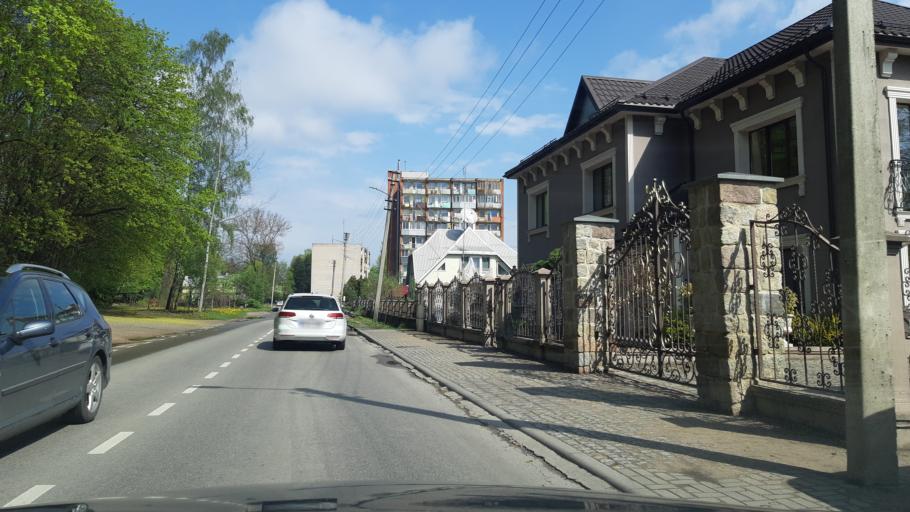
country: LT
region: Kauno apskritis
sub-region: Kaunas
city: Aleksotas
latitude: 54.8727
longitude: 23.9248
